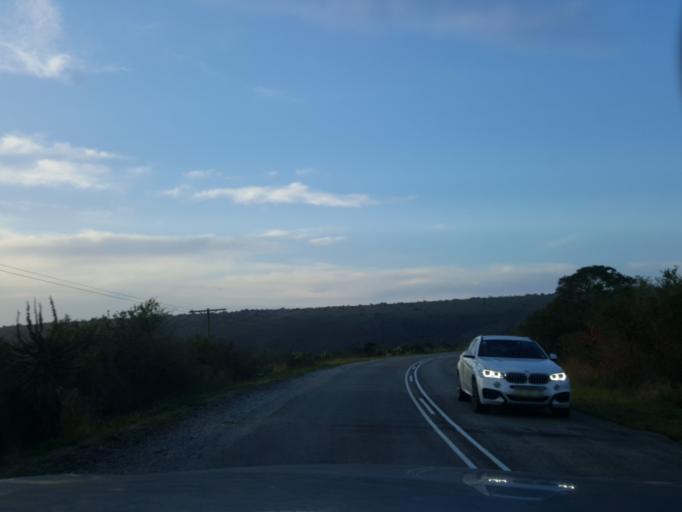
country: ZA
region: Eastern Cape
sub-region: Cacadu District Municipality
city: Grahamstown
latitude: -33.4649
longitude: 26.4816
